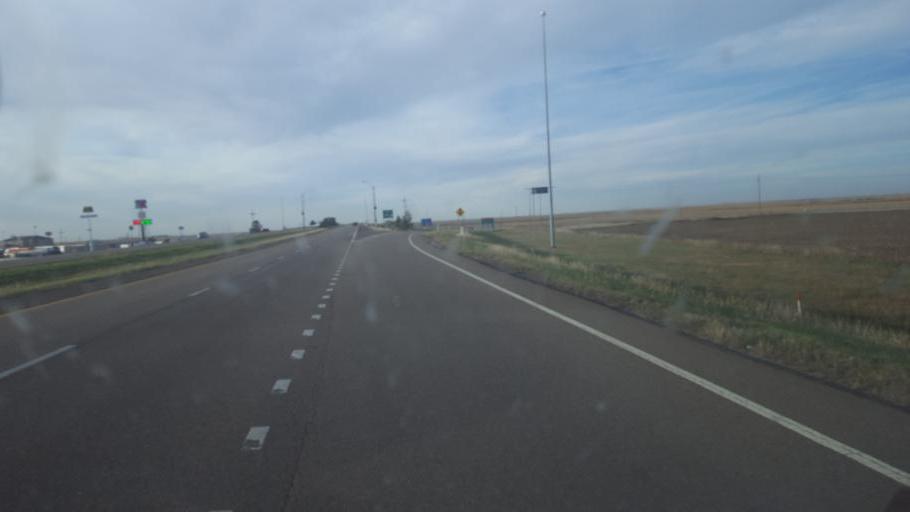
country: US
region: Kansas
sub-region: Logan County
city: Oakley
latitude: 39.1168
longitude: -100.8053
